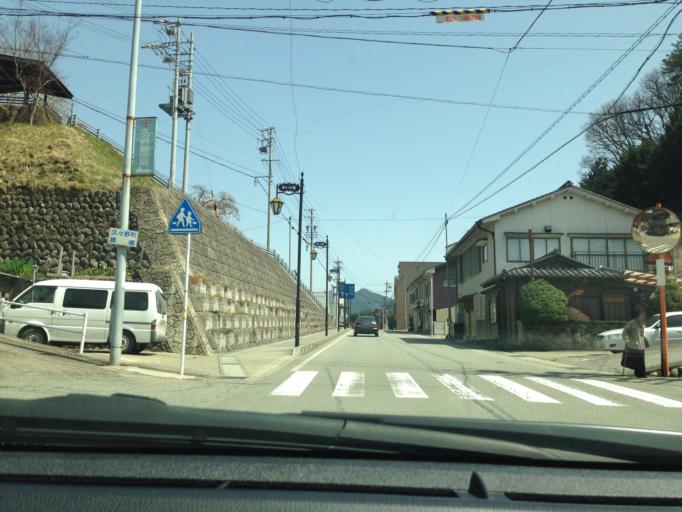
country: JP
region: Gifu
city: Takayama
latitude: 36.0501
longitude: 137.2757
